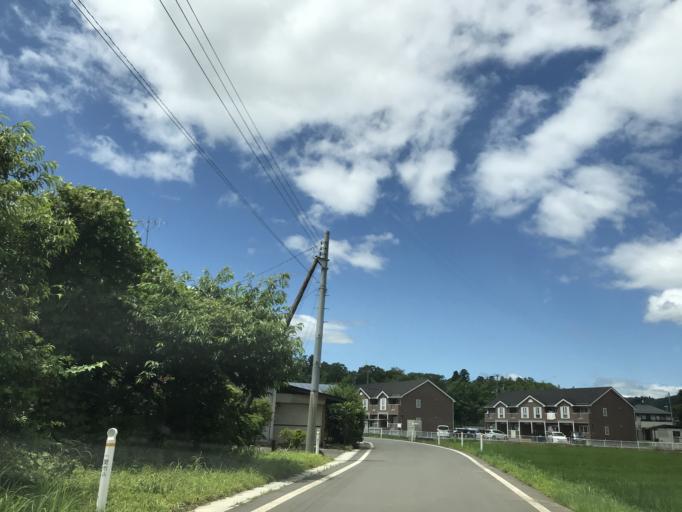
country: JP
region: Iwate
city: Ichinoseki
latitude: 38.9284
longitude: 141.0977
